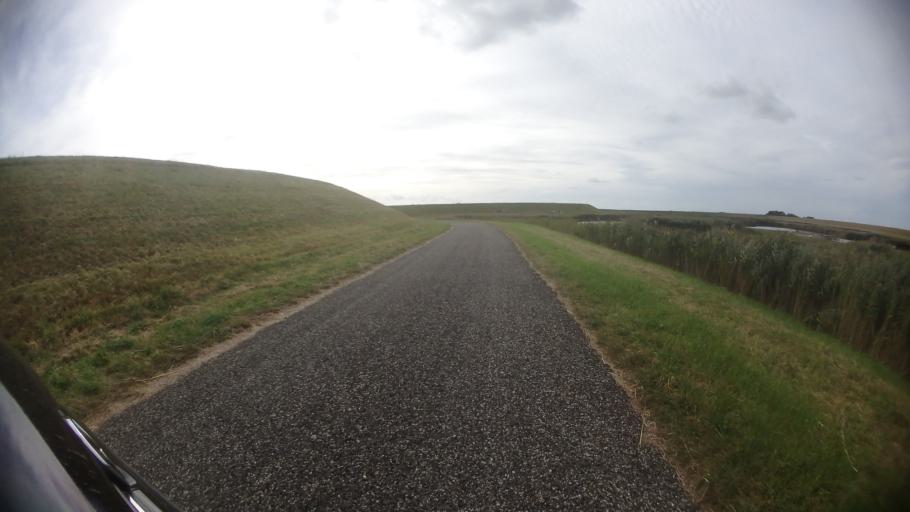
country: NL
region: North Holland
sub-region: Gemeente Texel
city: Den Burg
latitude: 53.0700
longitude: 4.8793
